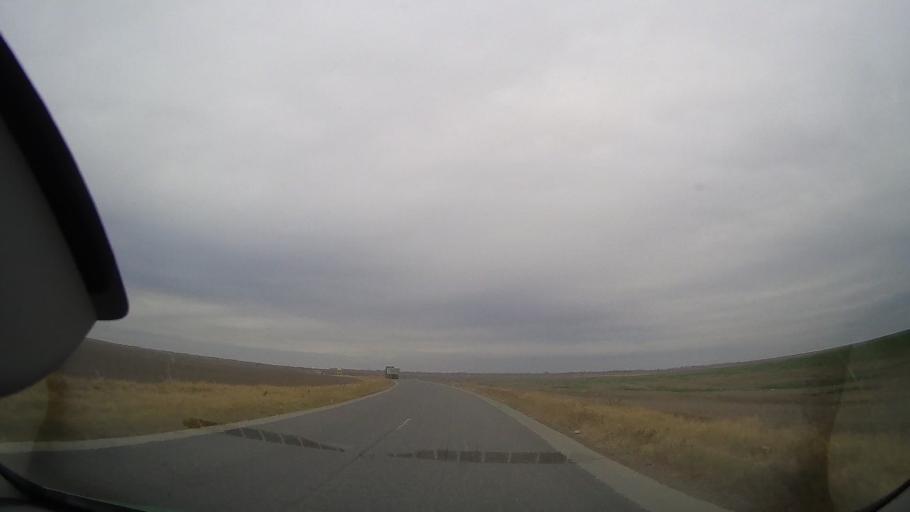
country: RO
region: Ialomita
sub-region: Comuna Milosesti
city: Milosesti
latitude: 44.7424
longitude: 27.2561
